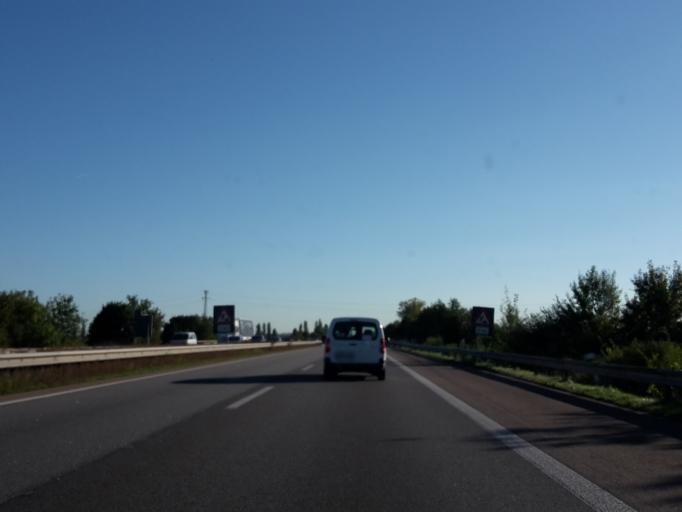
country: DE
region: Rheinland-Pfalz
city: Lambsheim
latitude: 49.5072
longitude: 8.3113
